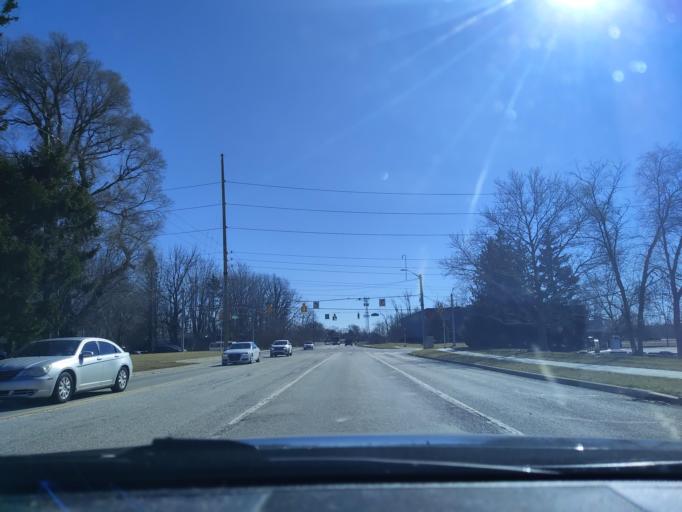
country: US
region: Indiana
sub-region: Boone County
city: Zionsville
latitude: 39.8974
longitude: -86.2410
